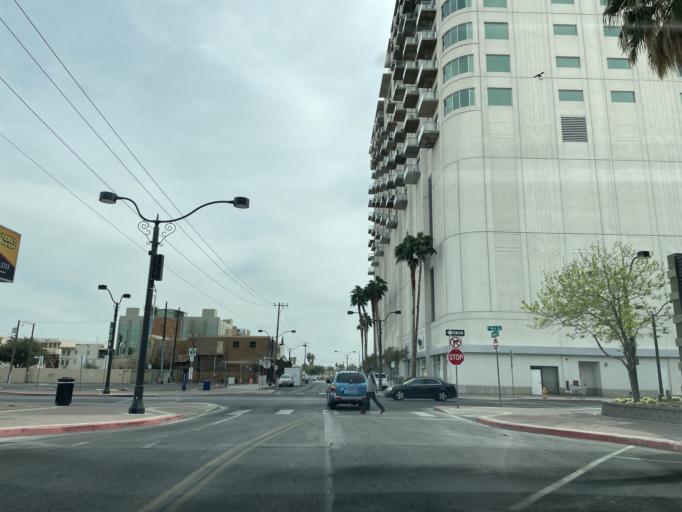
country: US
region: Nevada
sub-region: Clark County
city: Las Vegas
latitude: 36.1606
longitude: -115.1483
